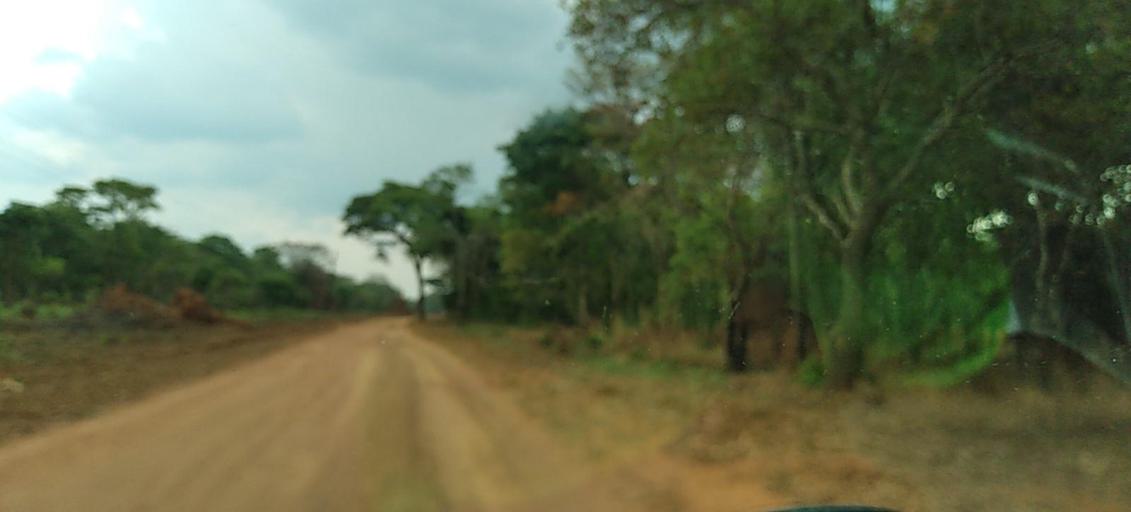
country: ZM
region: North-Western
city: Solwezi
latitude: -12.7811
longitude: 26.4918
